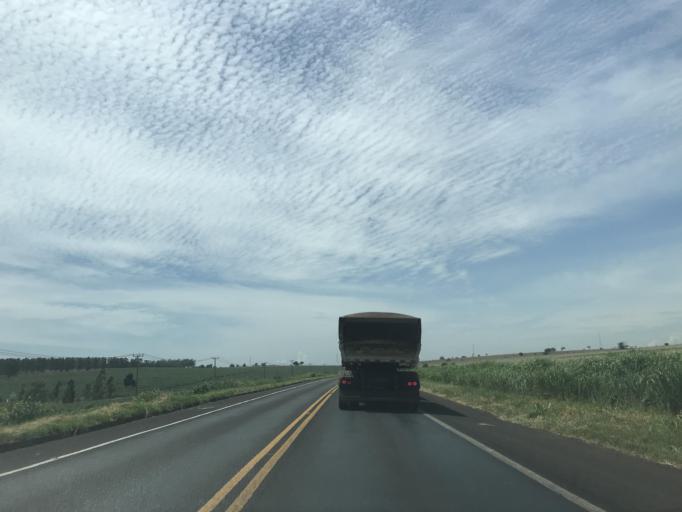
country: BR
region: Parana
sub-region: Paranavai
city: Paranavai
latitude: -23.0054
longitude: -52.5474
